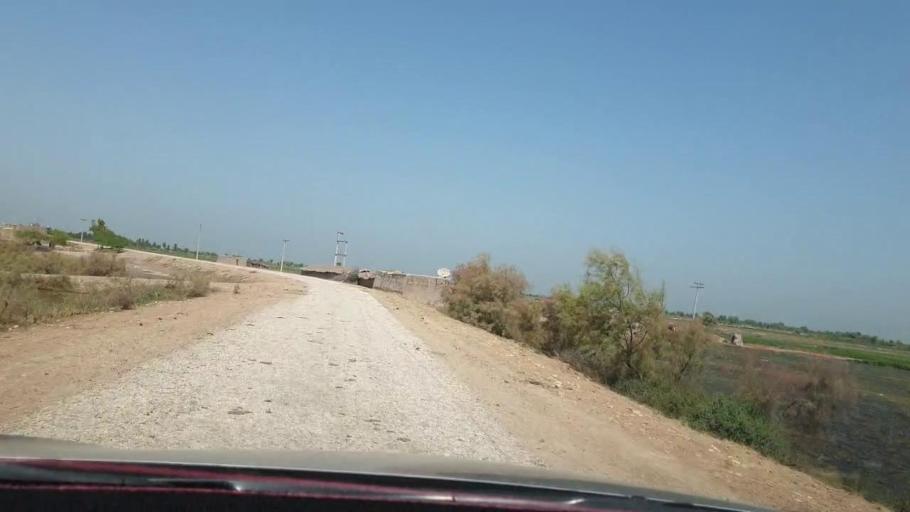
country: PK
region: Sindh
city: Warah
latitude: 27.5406
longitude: 67.7432
